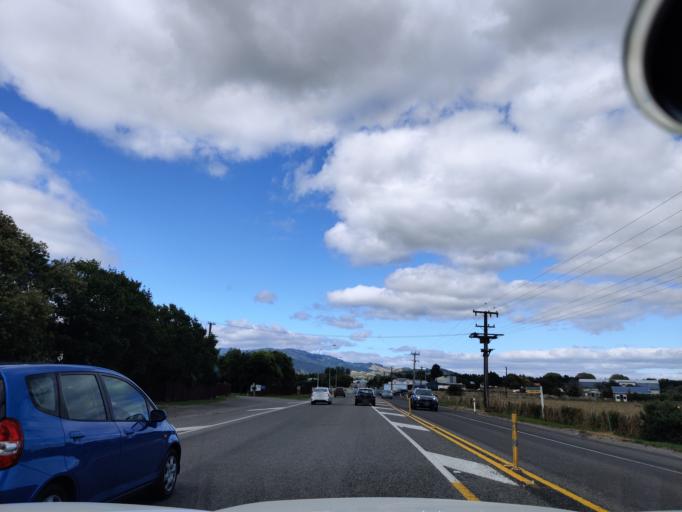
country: NZ
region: Manawatu-Wanganui
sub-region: Horowhenua District
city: Levin
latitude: -40.6787
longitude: 175.2401
